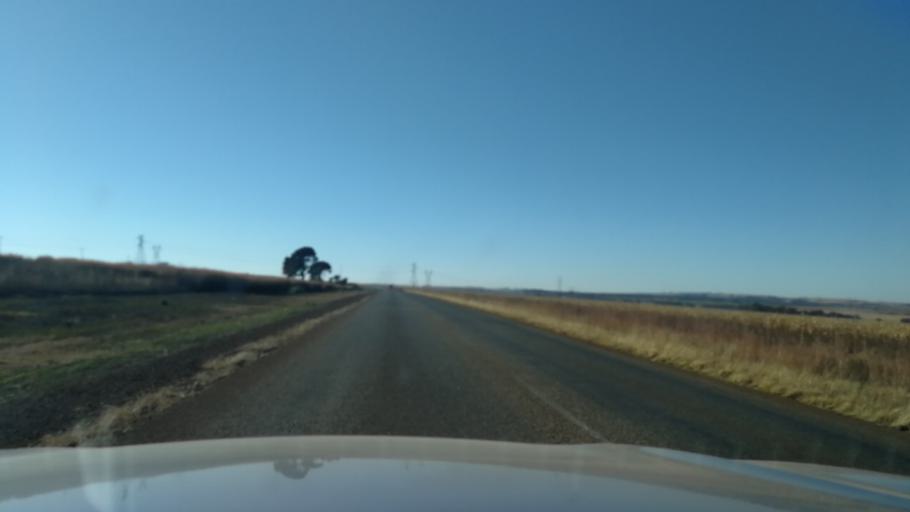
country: ZA
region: North-West
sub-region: Bojanala Platinum District Municipality
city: Rustenburg
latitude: -25.9941
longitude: 27.2930
